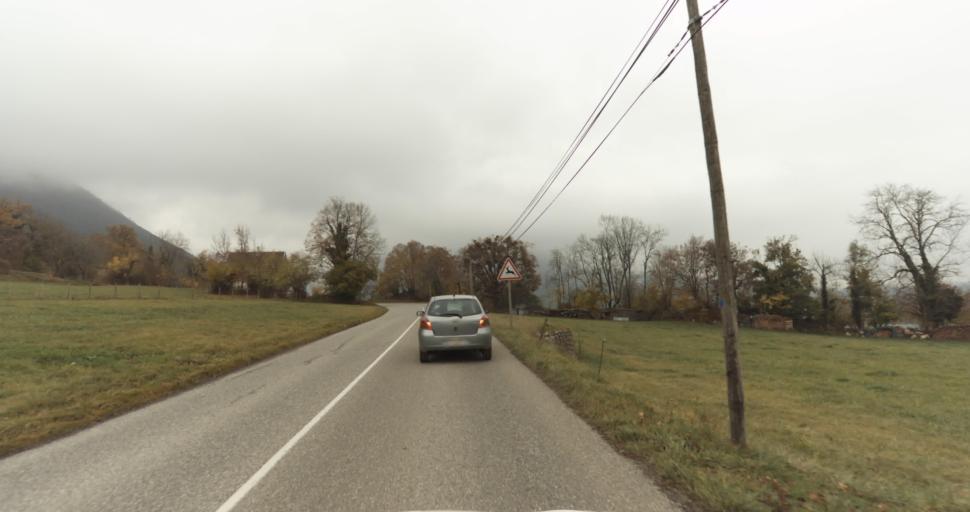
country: FR
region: Rhone-Alpes
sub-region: Departement de la Haute-Savoie
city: Gruffy
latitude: 45.7807
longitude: 6.0528
